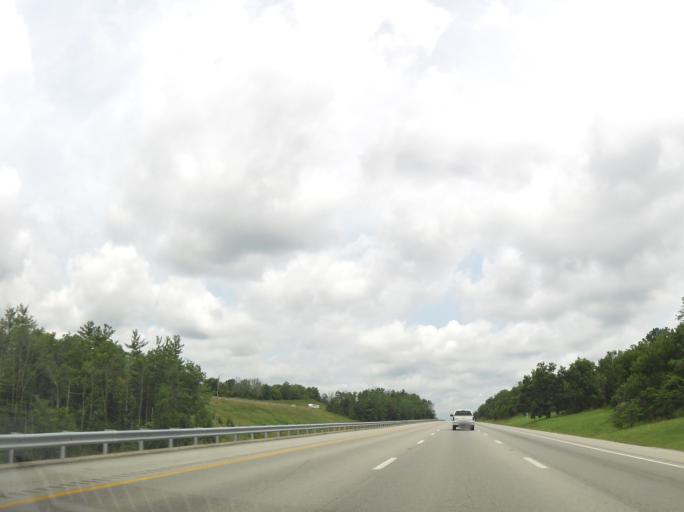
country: US
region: Kentucky
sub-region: Grant County
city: Williamstown
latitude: 38.4555
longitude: -84.5740
